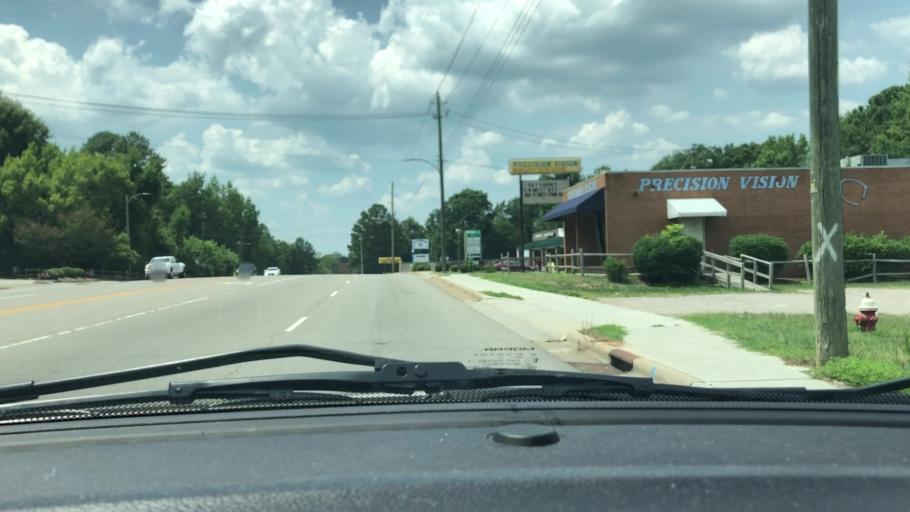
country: US
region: North Carolina
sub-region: Lee County
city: Sanford
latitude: 35.4716
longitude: -79.1736
